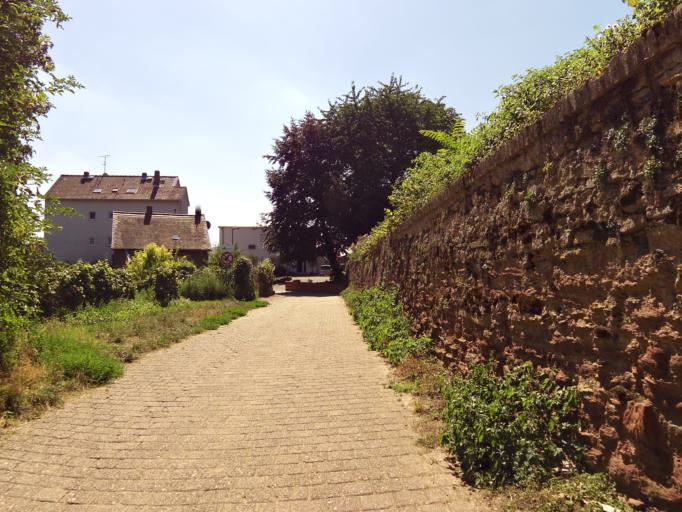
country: DE
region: Rheinland-Pfalz
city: Nierstein
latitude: 49.8798
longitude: 8.3388
